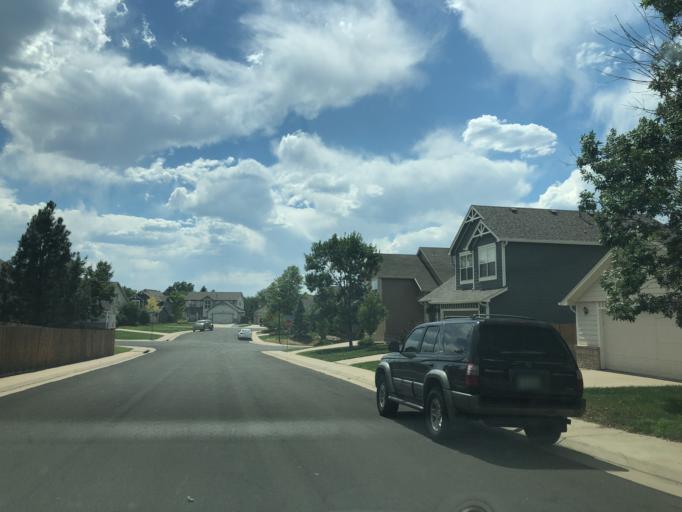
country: US
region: Colorado
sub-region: Arapahoe County
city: Dove Valley
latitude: 39.6215
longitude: -104.7706
